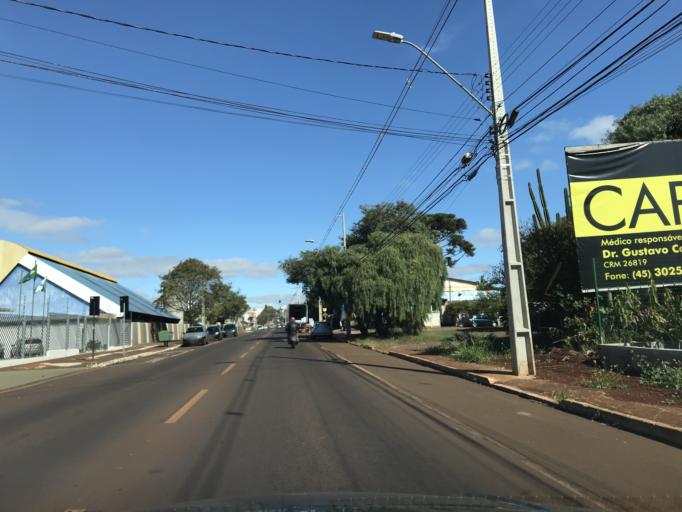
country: BR
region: Parana
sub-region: Cascavel
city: Cascavel
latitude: -24.9344
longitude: -53.4754
